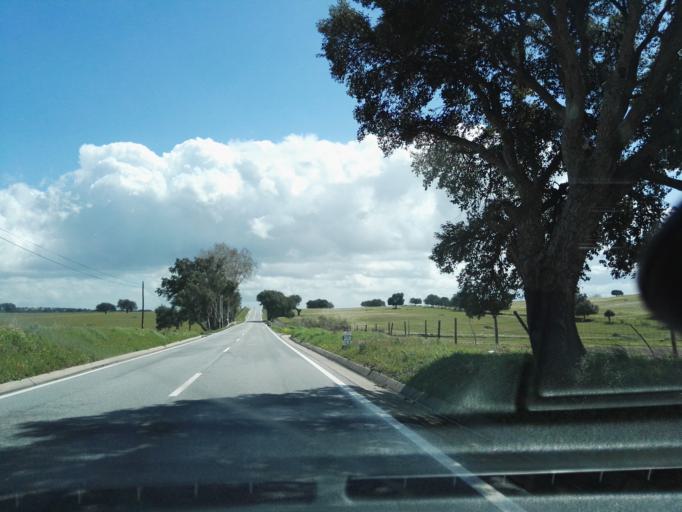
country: PT
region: Portalegre
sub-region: Arronches
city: Arronches
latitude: 39.1211
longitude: -7.2692
